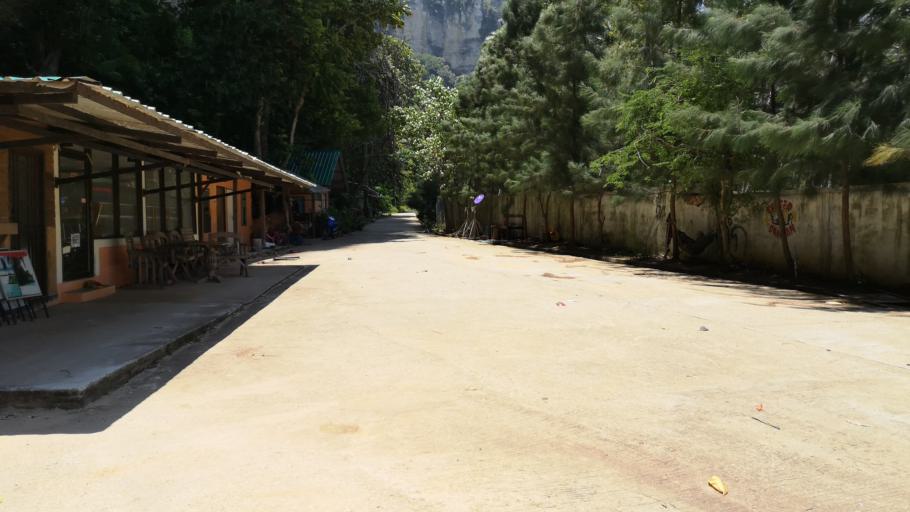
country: TH
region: Phangnga
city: Ban Ao Nang
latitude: 8.0184
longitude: 98.8310
